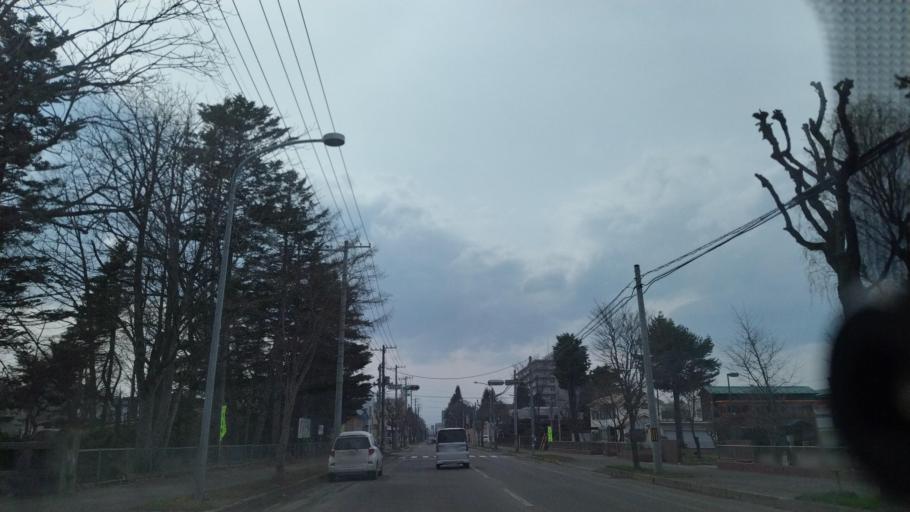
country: JP
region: Hokkaido
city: Obihiro
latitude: 42.9225
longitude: 143.2183
